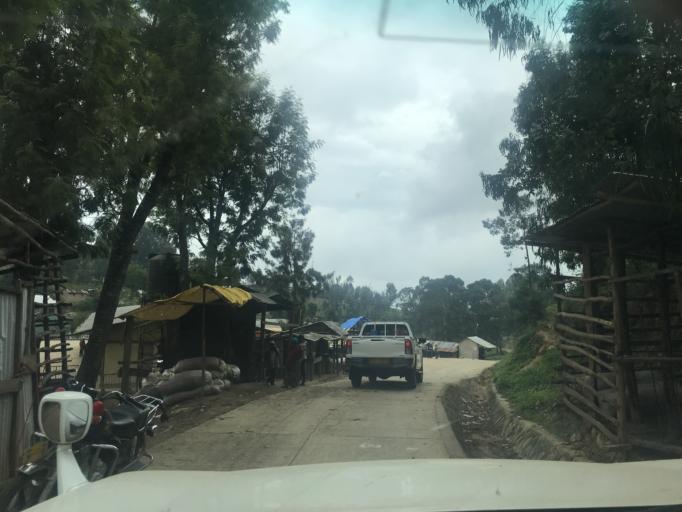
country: TZ
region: Morogoro
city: Morogoro
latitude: -7.0843
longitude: 37.5769
